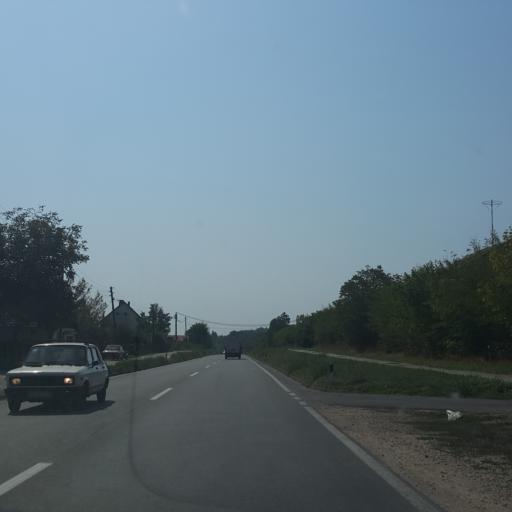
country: RS
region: Central Serbia
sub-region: Zajecarski Okrug
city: Zajecar
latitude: 43.8856
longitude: 22.2896
